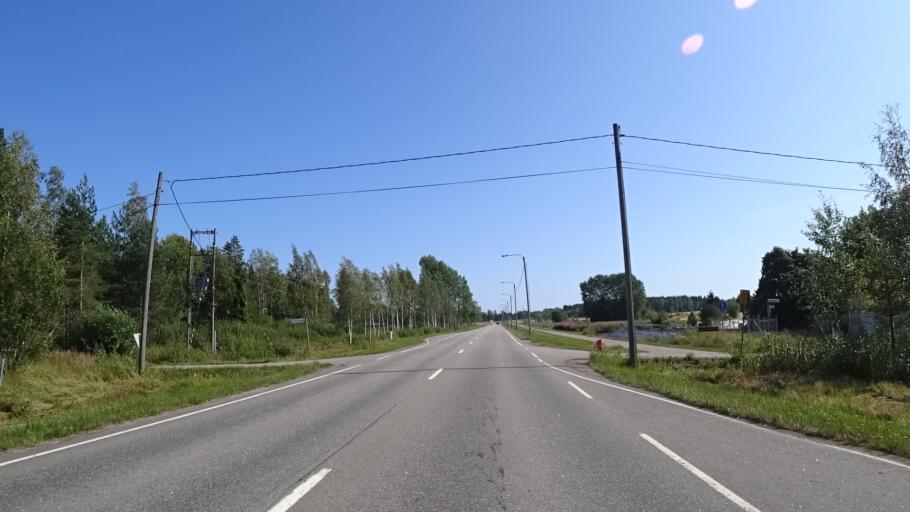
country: FI
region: Kymenlaakso
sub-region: Kotka-Hamina
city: Karhula
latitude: 60.5422
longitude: 26.9260
